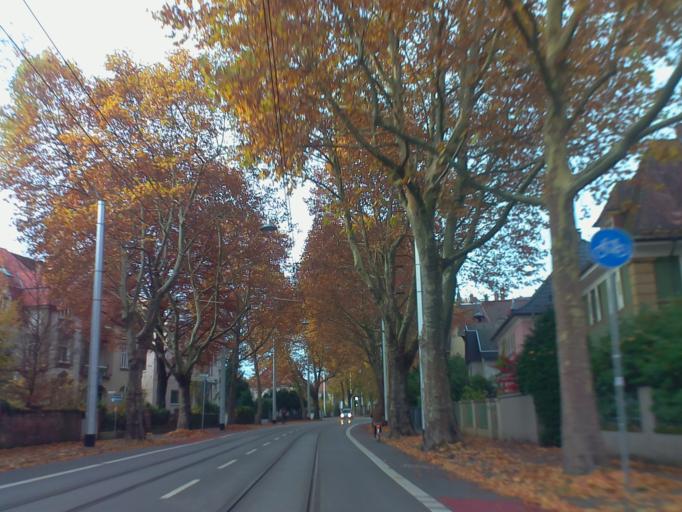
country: DE
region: Baden-Wuerttemberg
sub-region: Karlsruhe Region
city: Heidelberg
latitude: 49.4199
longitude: 8.6901
